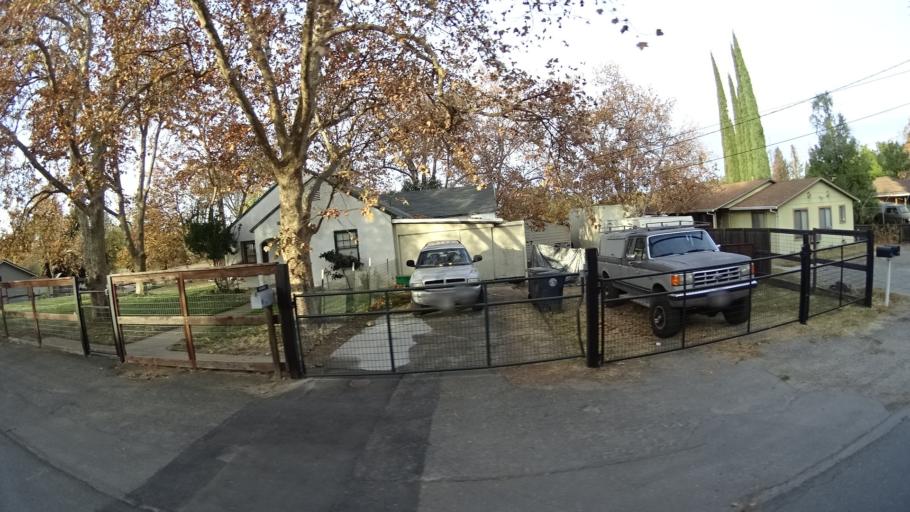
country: US
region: California
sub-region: Sacramento County
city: Citrus Heights
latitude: 38.7204
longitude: -121.2757
